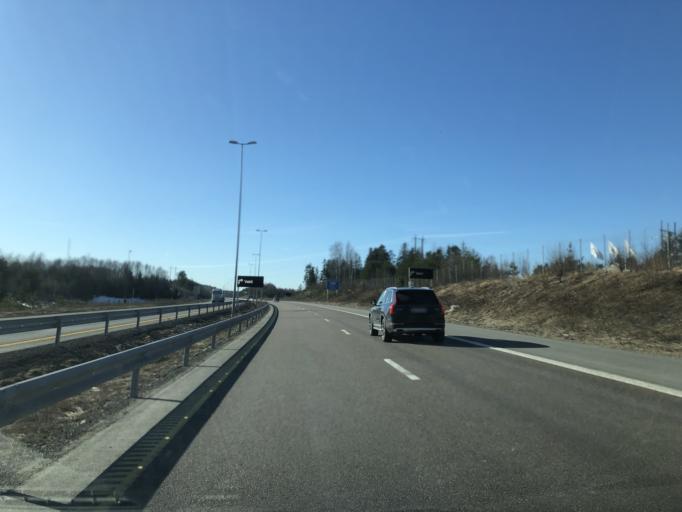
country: NO
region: Akershus
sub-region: Ullensaker
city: Jessheim
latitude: 60.1784
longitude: 11.1694
